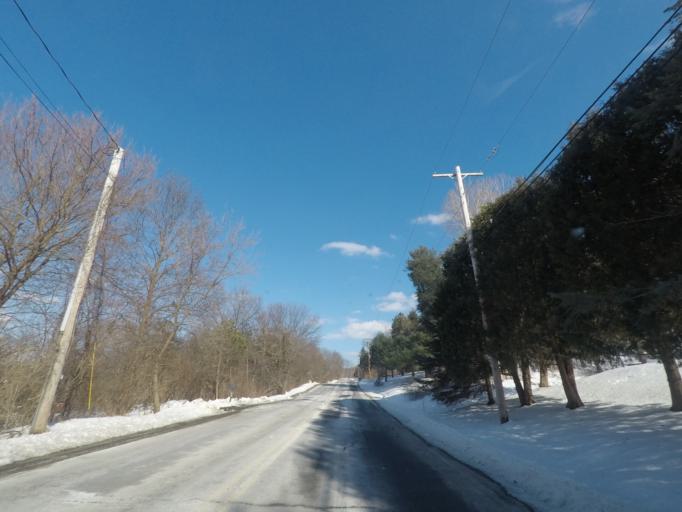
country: US
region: New York
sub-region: Saratoga County
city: Waterford
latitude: 42.7924
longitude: -73.6282
